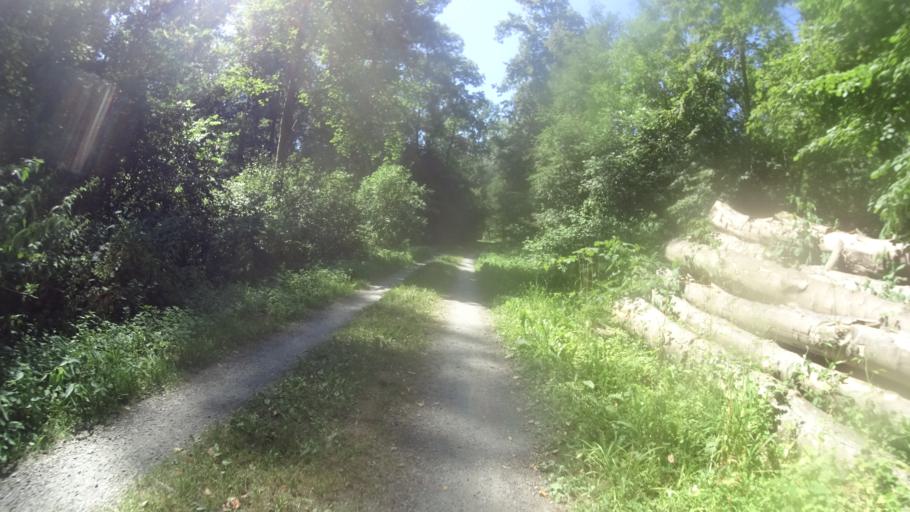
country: DE
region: Baden-Wuerttemberg
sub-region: Karlsruhe Region
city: Karlsruhe
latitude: 49.0130
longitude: 8.4588
